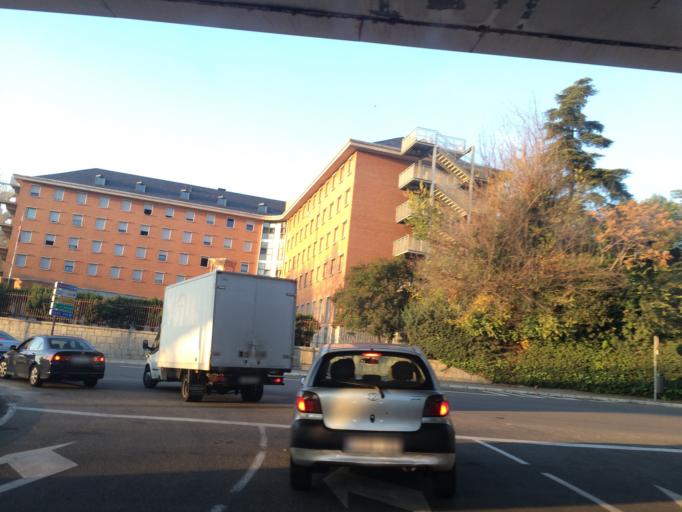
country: ES
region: Madrid
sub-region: Provincia de Madrid
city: Moncloa-Aravaca
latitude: 40.4341
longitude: -3.7341
